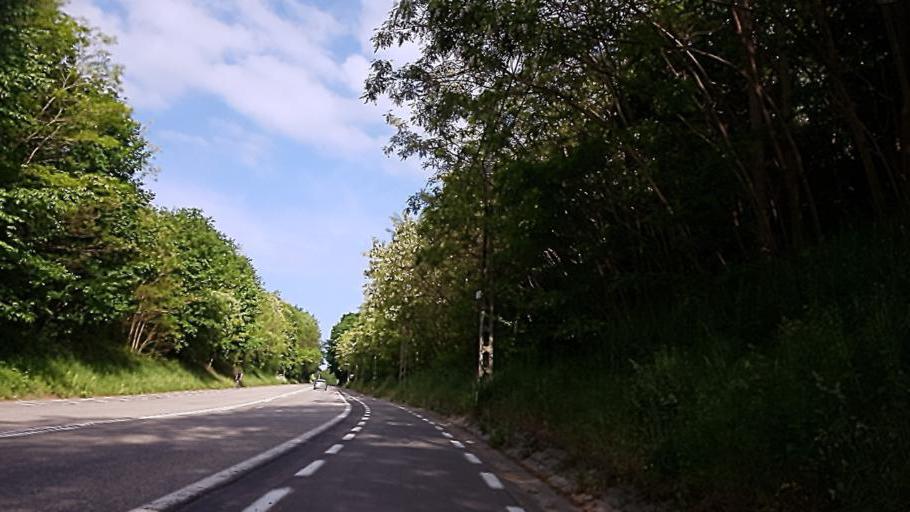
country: BE
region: Flanders
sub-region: Provincie Vlaams-Brabant
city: Huldenberg
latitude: 50.7575
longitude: 4.5685
